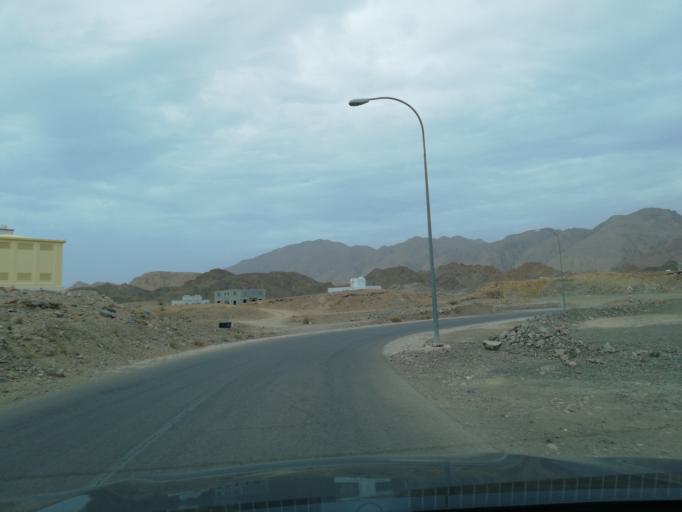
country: OM
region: Muhafazat Masqat
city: Bawshar
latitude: 23.4882
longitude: 58.3329
